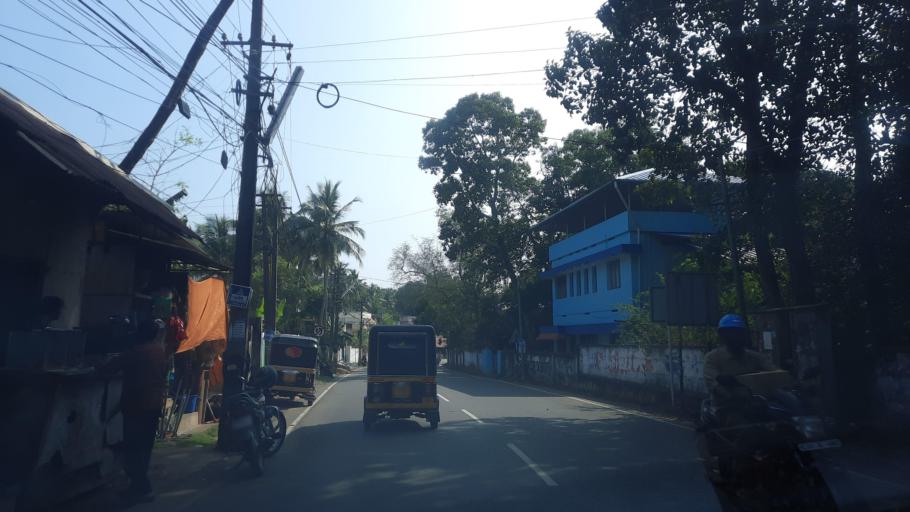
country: IN
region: Kerala
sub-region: Thiruvananthapuram
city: Nedumangad
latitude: 8.5724
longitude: 76.9252
